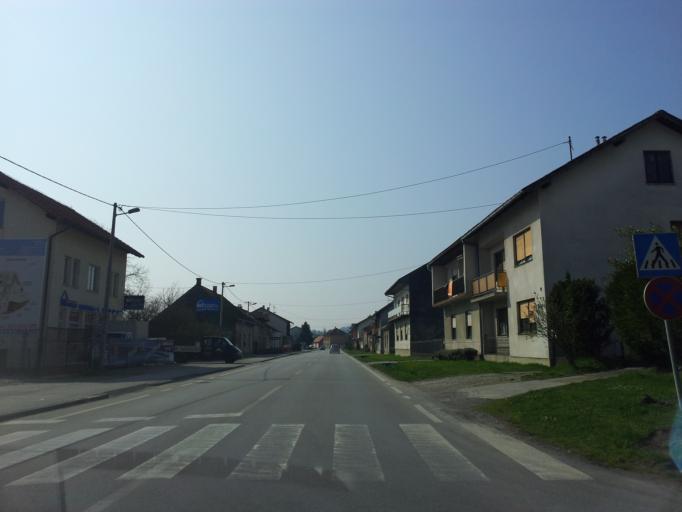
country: HR
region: Karlovacka
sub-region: Grad Karlovac
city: Karlovac
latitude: 45.4722
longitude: 15.5597
